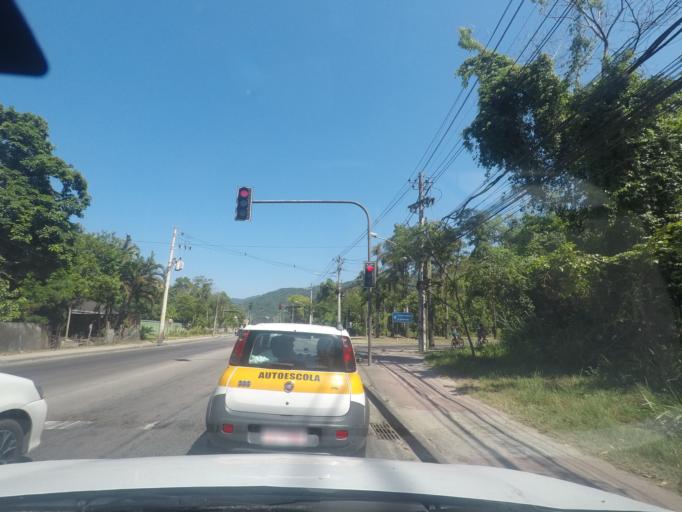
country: BR
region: Rio de Janeiro
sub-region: Nilopolis
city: Nilopolis
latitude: -22.9888
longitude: -43.4542
